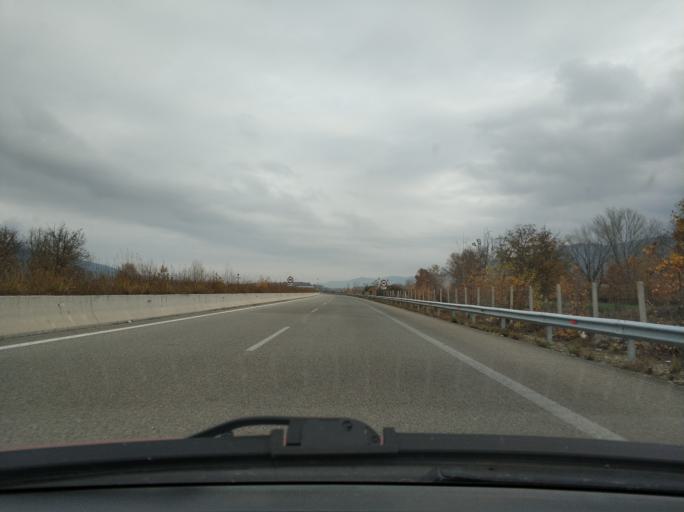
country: GR
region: East Macedonia and Thrace
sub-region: Nomos Kavalas
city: Palaiochori
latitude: 40.8542
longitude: 24.1534
